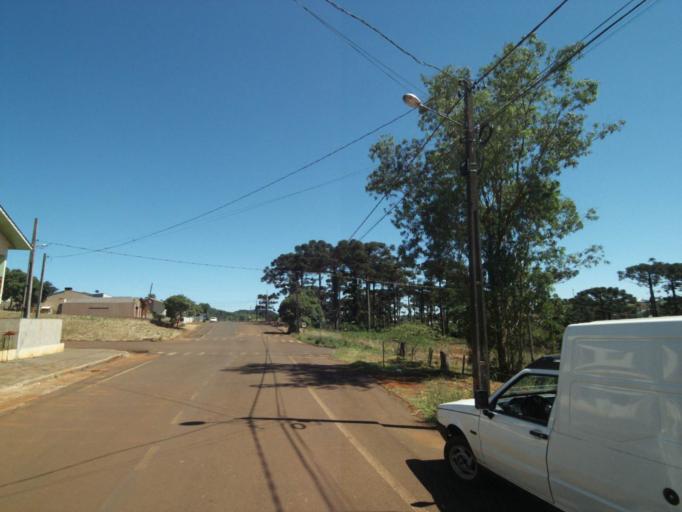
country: BR
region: Santa Catarina
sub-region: Sao Lourenco Do Oeste
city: Sao Lourenco dOeste
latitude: -26.2705
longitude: -52.7798
